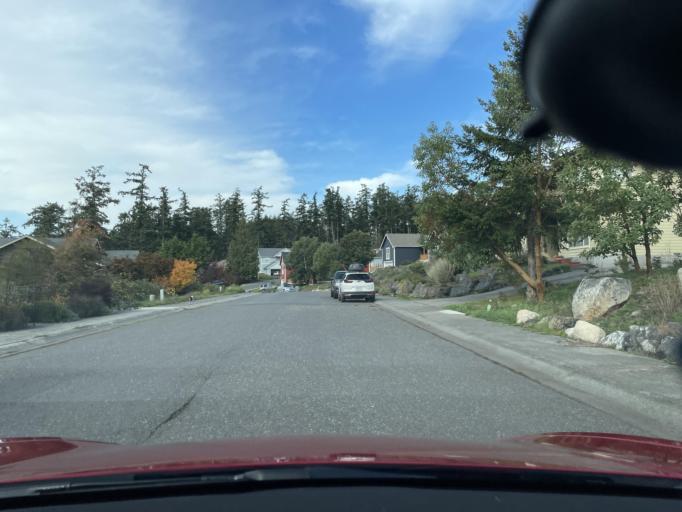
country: US
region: Washington
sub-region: San Juan County
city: Friday Harbor
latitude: 48.5418
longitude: -123.0320
